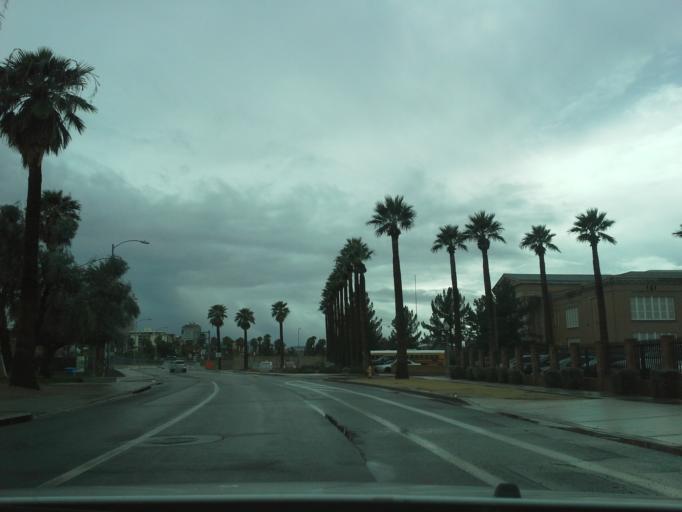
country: US
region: Arizona
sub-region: Maricopa County
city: Phoenix
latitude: 33.4633
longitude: -112.0803
